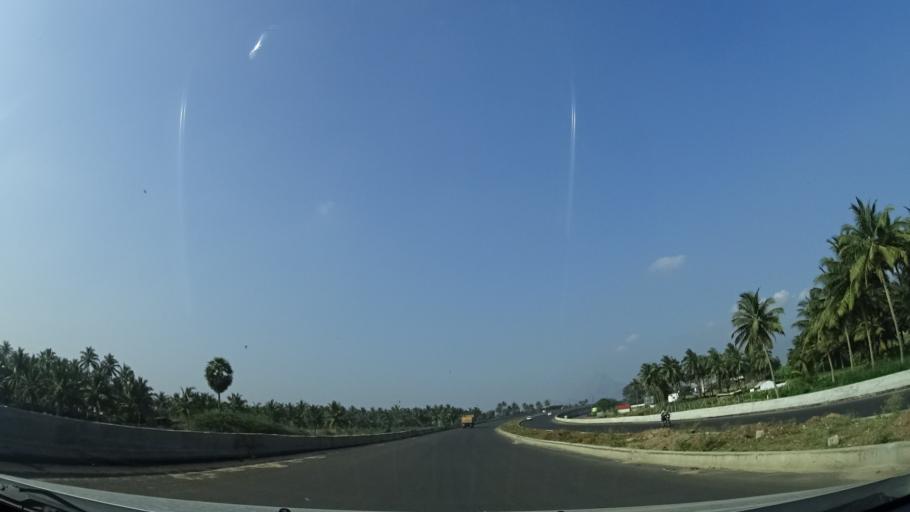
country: IN
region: Tamil Nadu
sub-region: Coimbatore
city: Madukkarai
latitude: 10.8731
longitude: 76.9025
